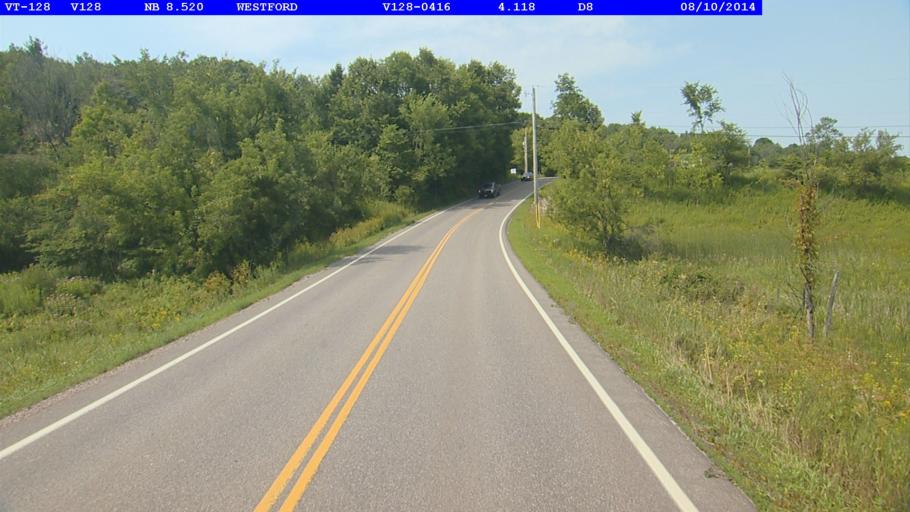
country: US
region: Vermont
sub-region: Chittenden County
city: Milton
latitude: 44.6140
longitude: -73.0140
